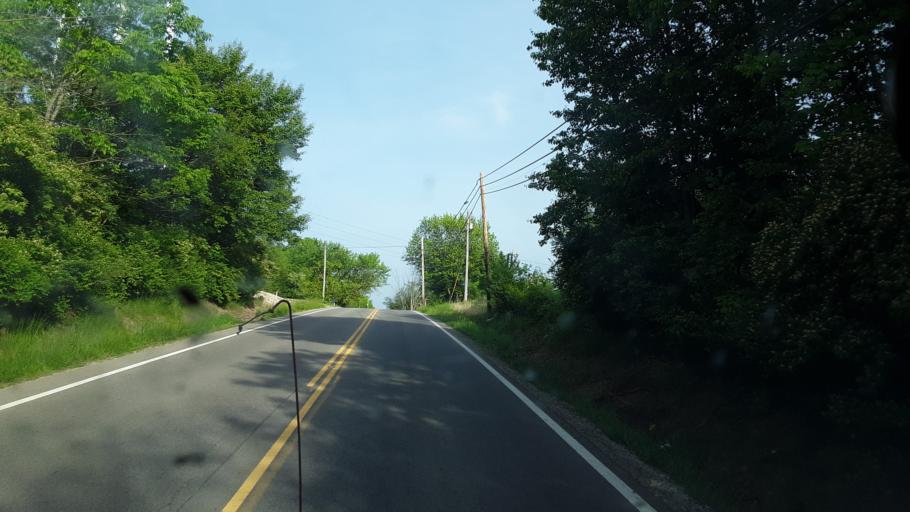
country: US
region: Ohio
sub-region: Pickaway County
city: Logan Elm Village
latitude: 39.5752
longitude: -82.8979
